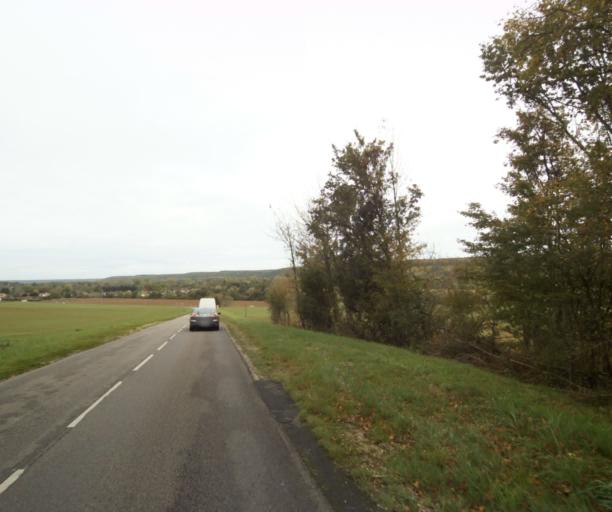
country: FR
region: Centre
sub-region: Departement d'Eure-et-Loir
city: Dreux
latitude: 48.7692
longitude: 1.3702
